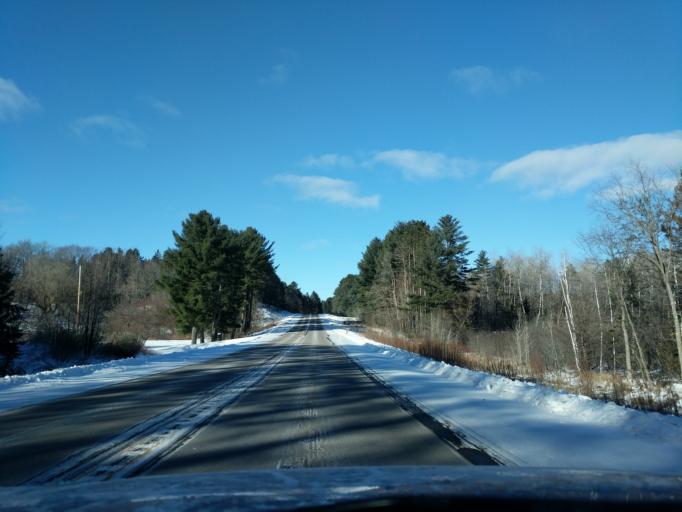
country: US
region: Wisconsin
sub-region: Menominee County
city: Keshena
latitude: 45.1382
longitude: -88.6767
